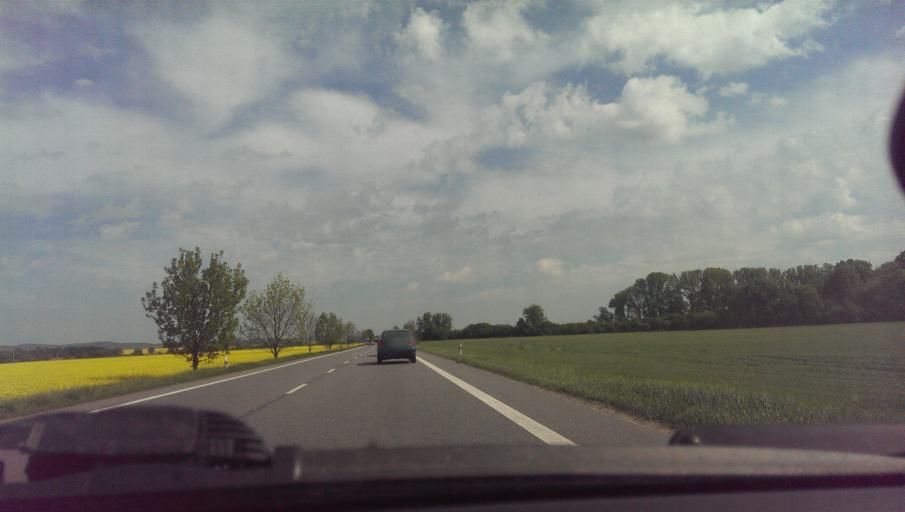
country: CZ
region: Zlin
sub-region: Okres Uherske Hradiste
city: Uherske Hradiste
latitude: 49.0962
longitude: 17.4535
